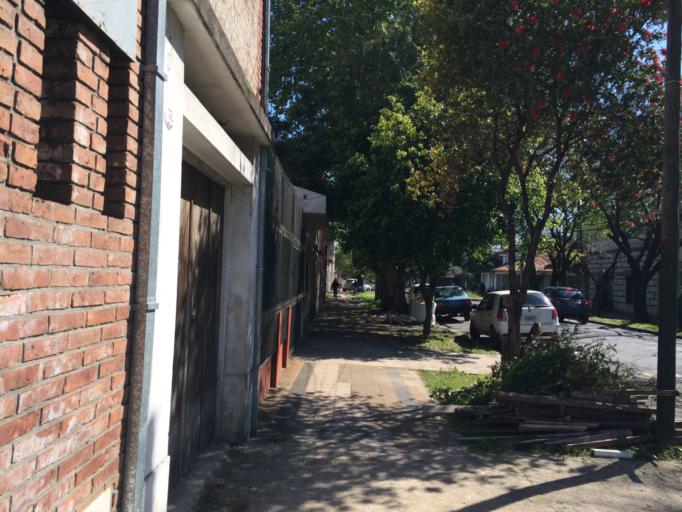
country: AR
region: Buenos Aires
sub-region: Partido de Lomas de Zamora
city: Lomas de Zamora
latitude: -34.7572
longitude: -58.3943
